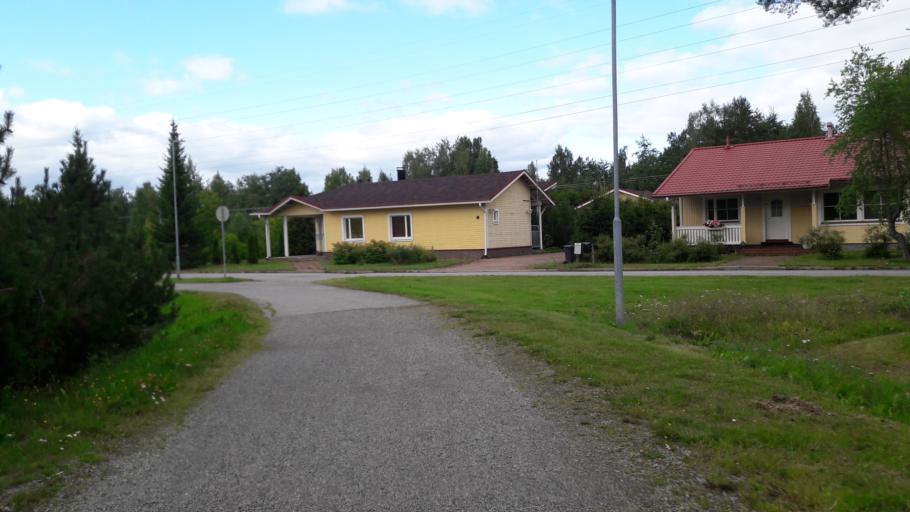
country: FI
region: North Karelia
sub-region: Joensuu
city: Joensuu
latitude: 62.5955
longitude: 29.7959
